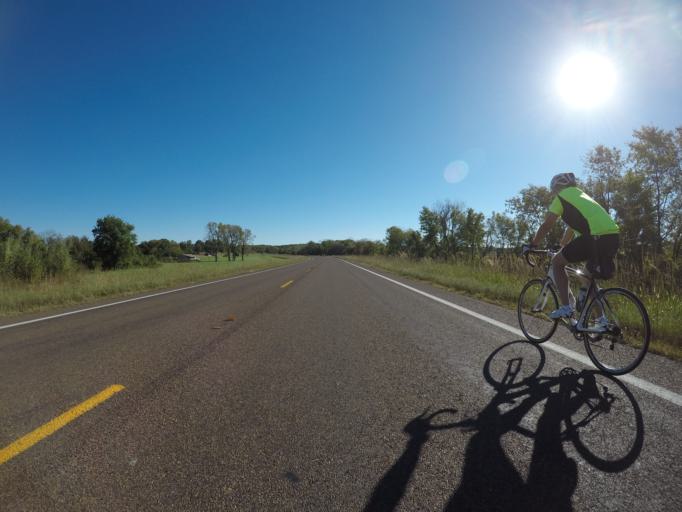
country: US
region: Kansas
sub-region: Johnson County
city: De Soto
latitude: 39.0069
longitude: -95.0234
